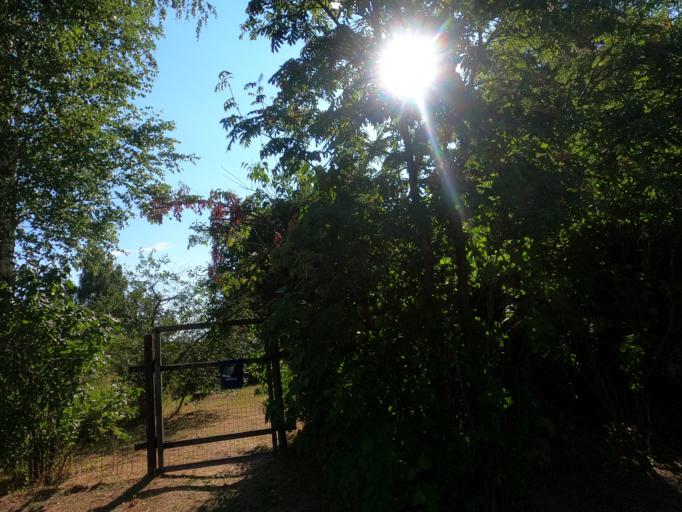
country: RU
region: Moskovskaya
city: Konobeyevo
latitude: 55.4119
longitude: 38.6960
